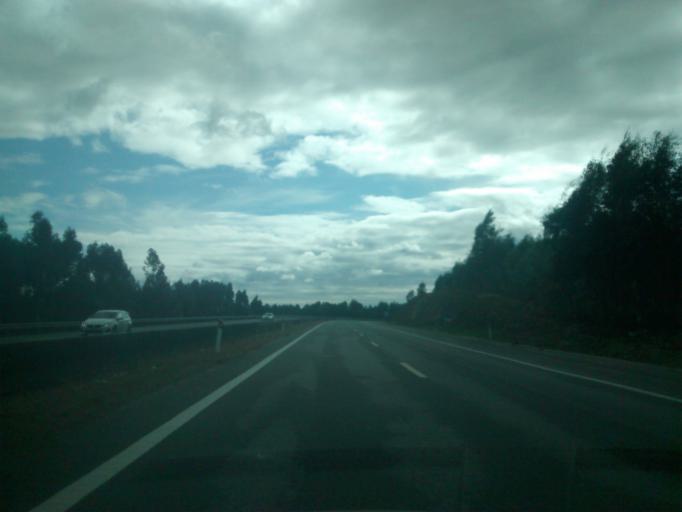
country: PT
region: Aveiro
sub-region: Agueda
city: Valongo
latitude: 40.6656
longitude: -8.4135
